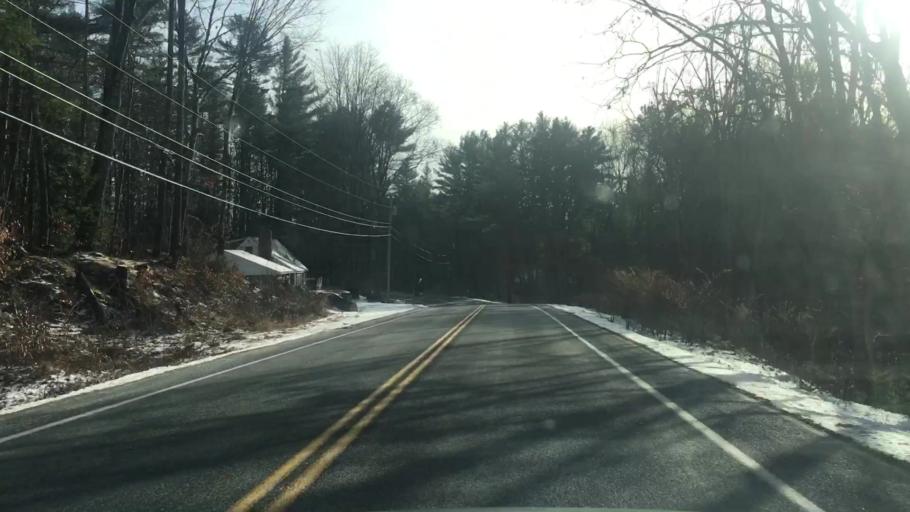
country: US
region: New Hampshire
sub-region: Merrimack County
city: Canterbury
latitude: 43.2976
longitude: -71.5636
